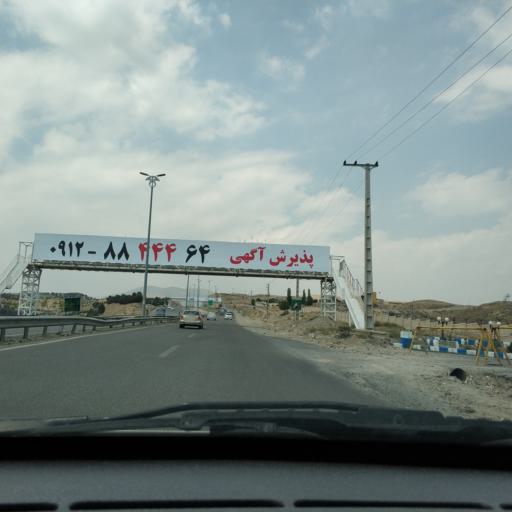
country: IR
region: Tehran
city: Tajrish
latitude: 35.7805
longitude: 51.5631
